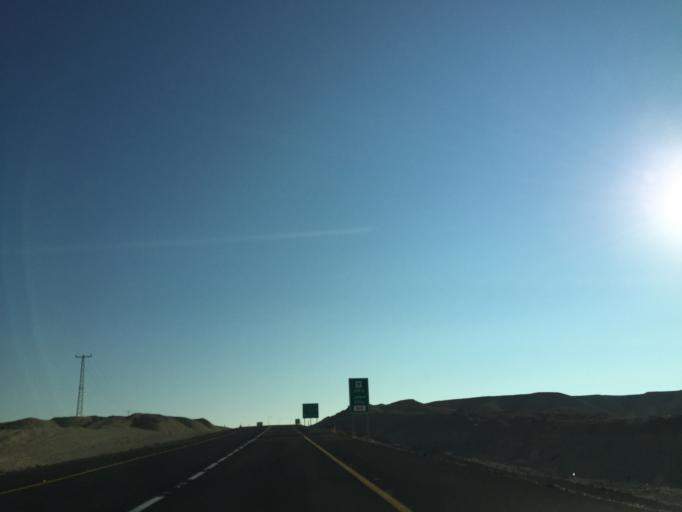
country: IL
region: Southern District
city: Mitzpe Ramon
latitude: 30.2779
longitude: 35.0146
